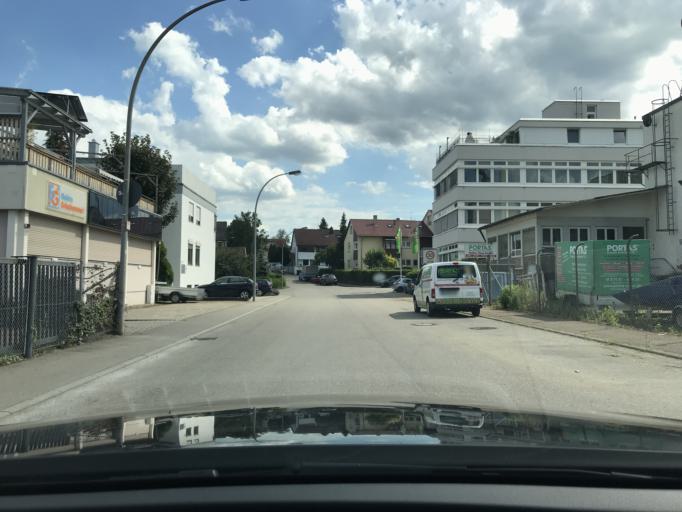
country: DE
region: Baden-Wuerttemberg
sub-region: Regierungsbezirk Stuttgart
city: Waiblingen
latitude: 48.8139
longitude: 9.3206
